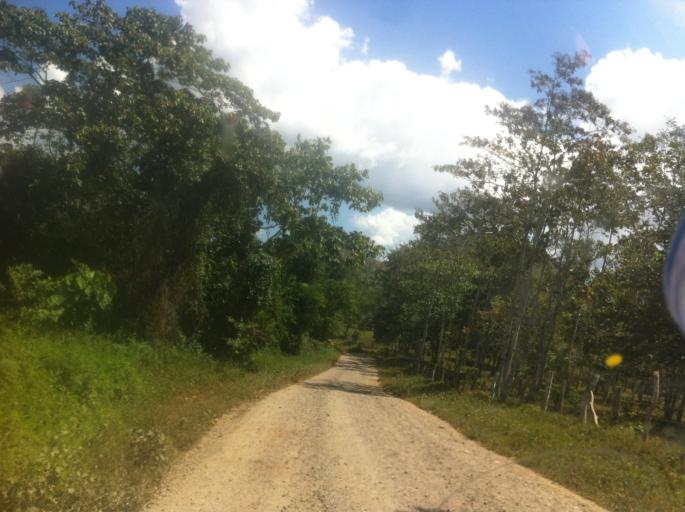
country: CR
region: Alajuela
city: Los Chiles
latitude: 11.2374
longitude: -84.5094
